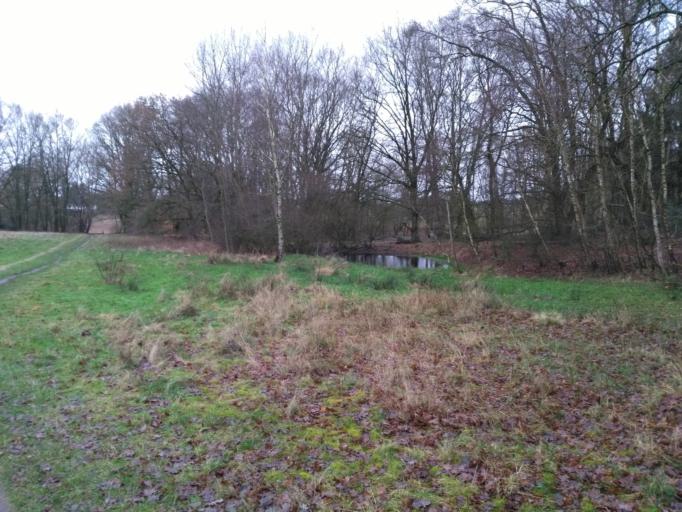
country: DE
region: Lower Saxony
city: Neu Wulmstorf
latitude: 53.4650
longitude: 9.8224
